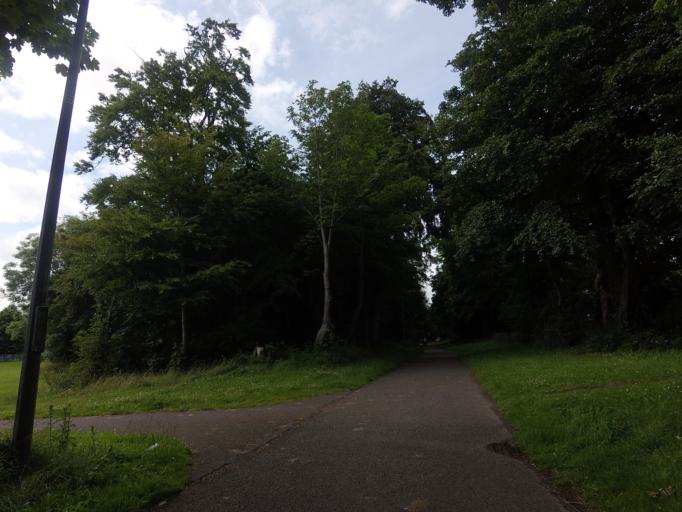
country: IE
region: Leinster
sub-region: Fingal County
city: Blanchardstown
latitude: 53.3844
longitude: -6.3939
